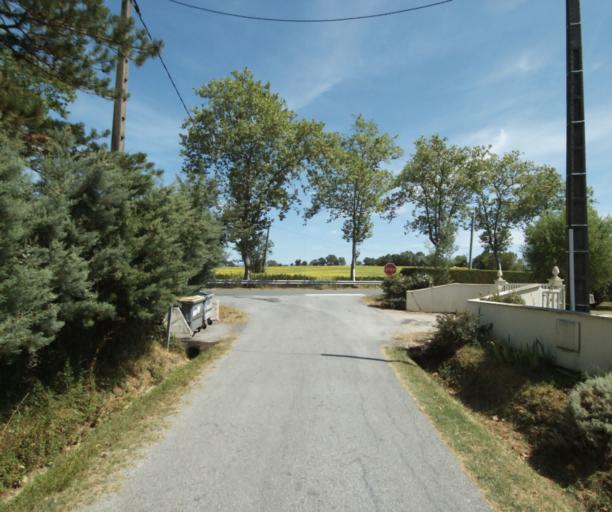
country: FR
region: Midi-Pyrenees
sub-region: Departement de la Haute-Garonne
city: Revel
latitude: 43.5056
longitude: 2.0110
